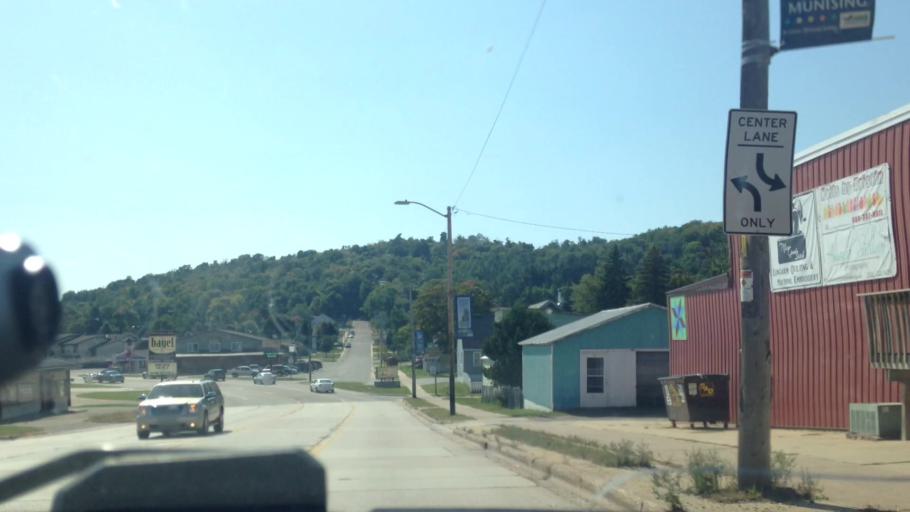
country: US
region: Michigan
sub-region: Alger County
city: Munising
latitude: 46.4087
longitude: -86.6507
